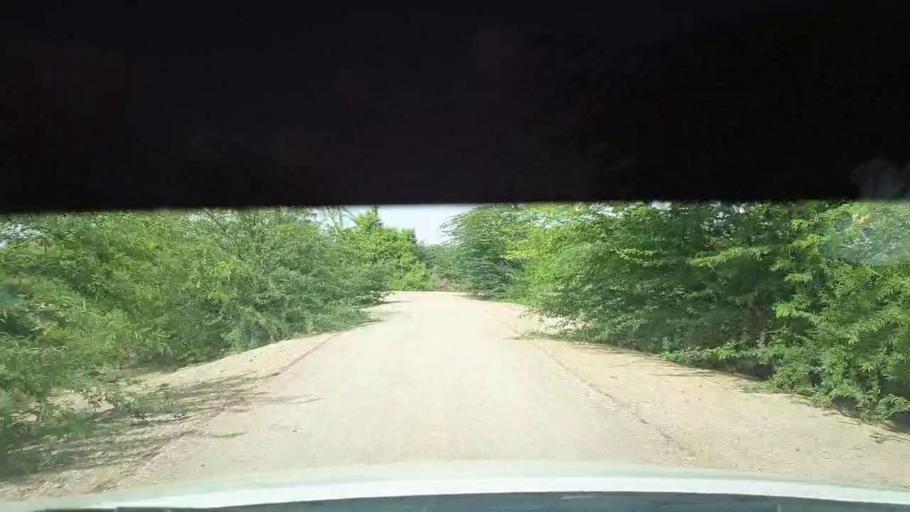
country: PK
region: Sindh
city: Kadhan
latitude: 24.5341
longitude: 69.0409
